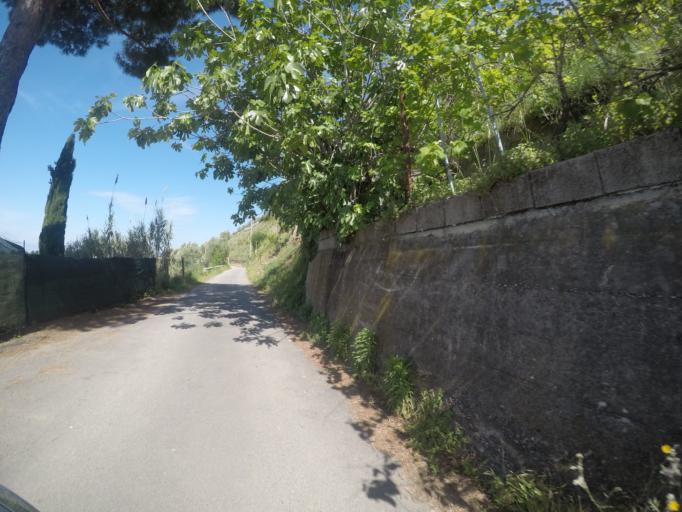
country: IT
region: Tuscany
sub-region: Provincia di Massa-Carrara
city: Massa
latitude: 44.0507
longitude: 10.0997
